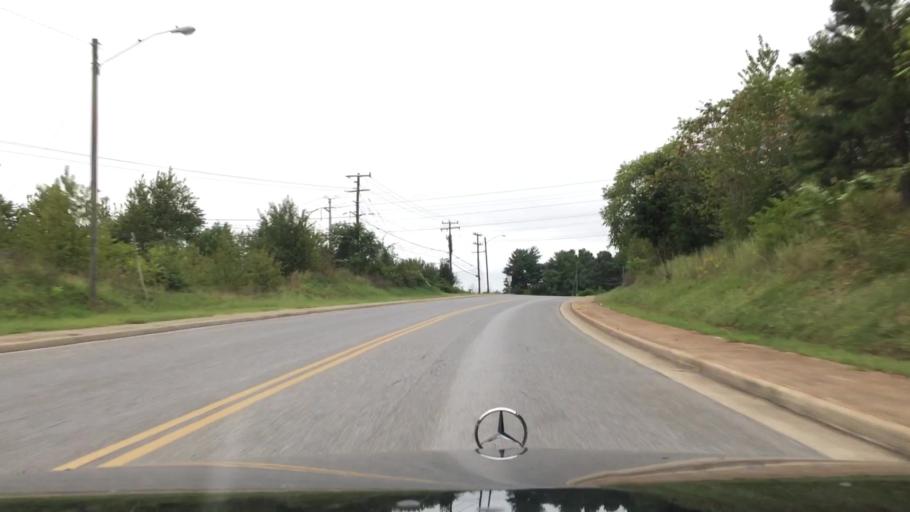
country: US
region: Virginia
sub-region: Campbell County
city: Altavista
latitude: 37.1205
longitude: -79.2762
